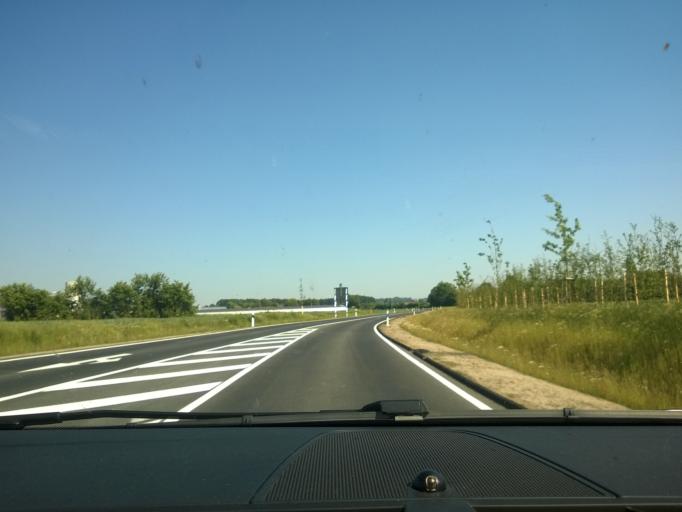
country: DE
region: North Rhine-Westphalia
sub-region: Regierungsbezirk Munster
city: Nottuln
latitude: 51.9194
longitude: 7.3814
